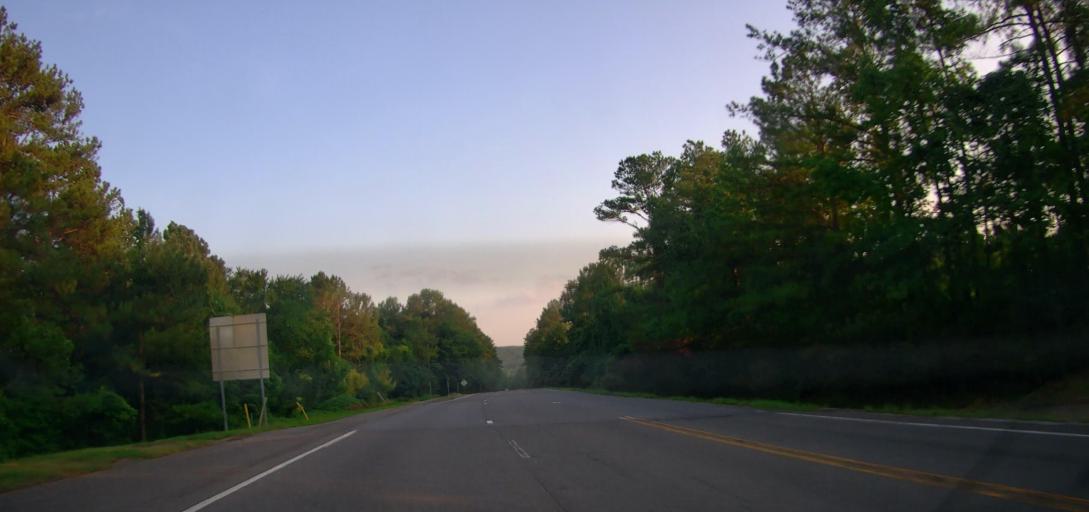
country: US
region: Alabama
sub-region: Marion County
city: Hamilton
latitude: 34.0807
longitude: -87.9764
